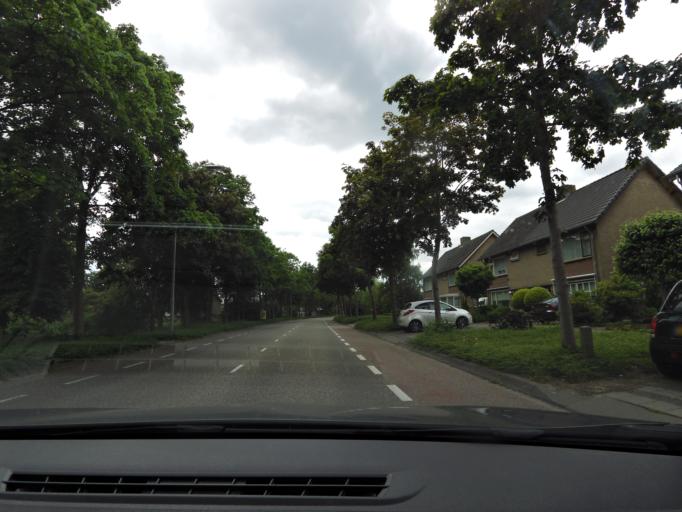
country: NL
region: North Brabant
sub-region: Gemeente Made en Drimmelen
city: Made
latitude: 51.6711
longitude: 4.7888
